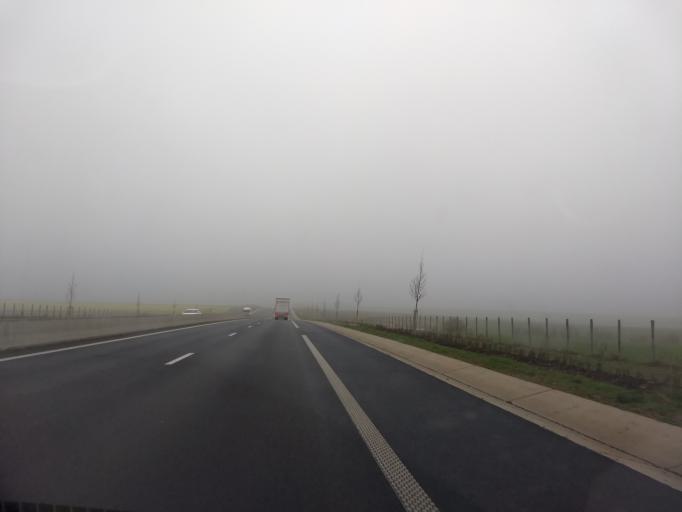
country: FR
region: Nord-Pas-de-Calais
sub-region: Departement du Pas-de-Calais
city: Aubigny-en-Artois
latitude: 50.3390
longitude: 2.6099
